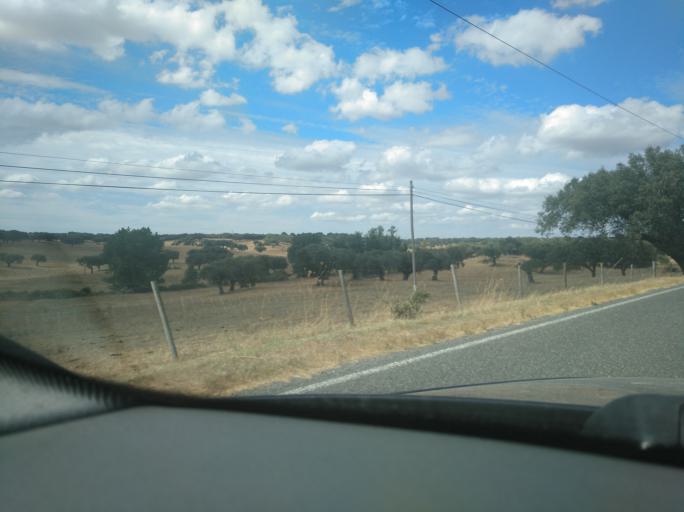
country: PT
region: Portalegre
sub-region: Arronches
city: Arronches
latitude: 39.0915
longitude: -7.3420
